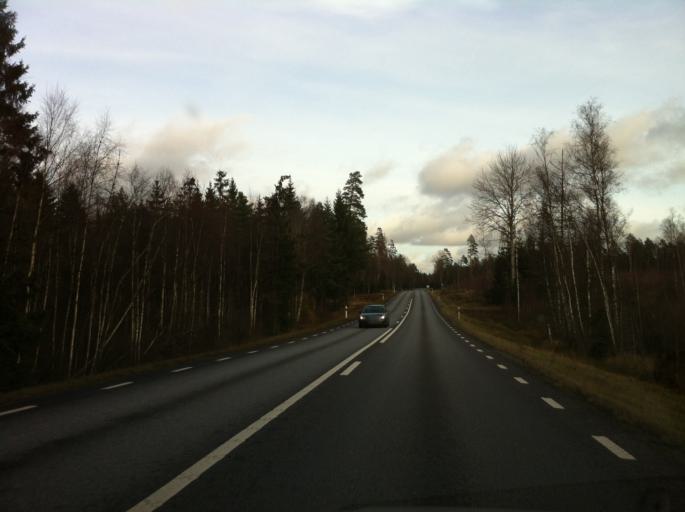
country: SE
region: Kronoberg
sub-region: Alvesta Kommun
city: Vislanda
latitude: 56.7636
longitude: 14.5258
